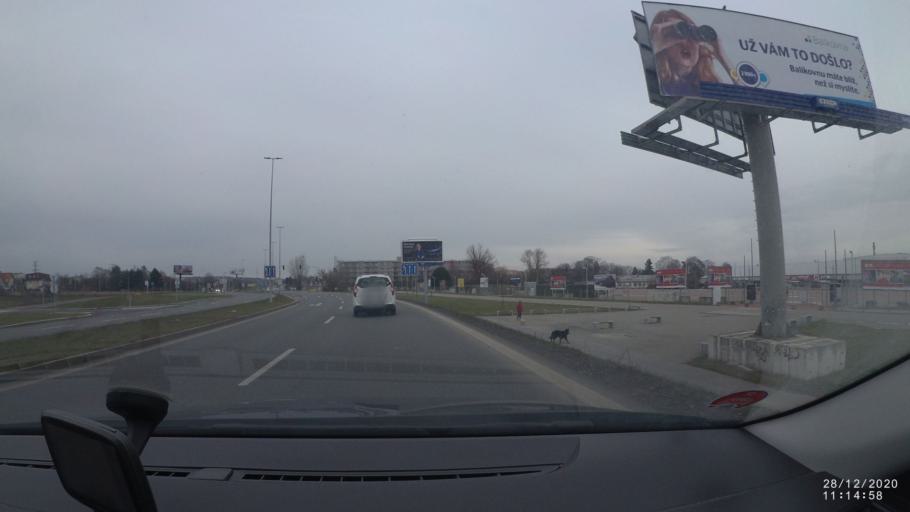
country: CZ
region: Praha
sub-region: Praha 18
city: Letnany
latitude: 50.1281
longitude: 14.5139
